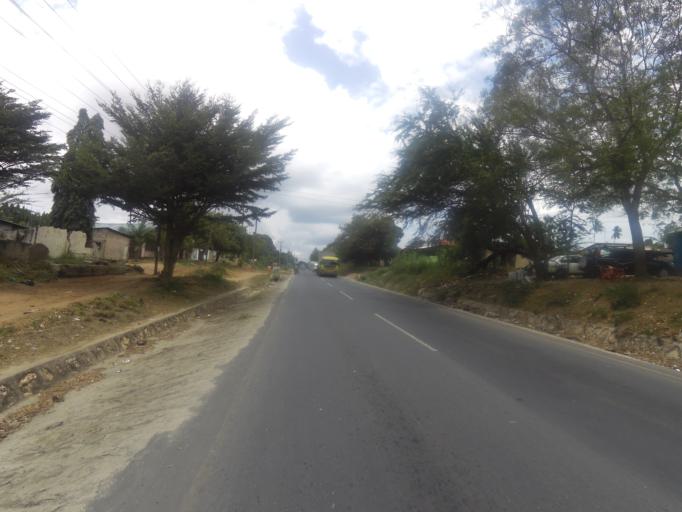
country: TZ
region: Pwani
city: Vikindu
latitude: -6.9570
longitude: 39.2837
